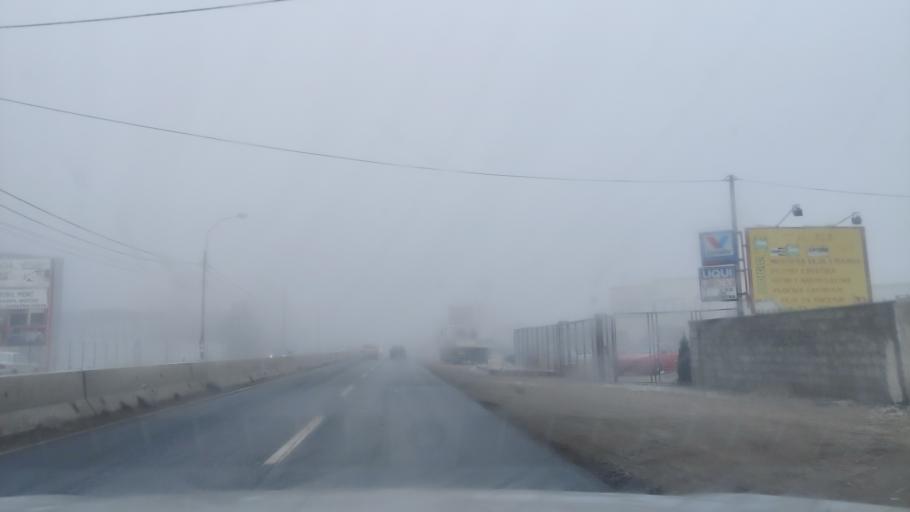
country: RS
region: Central Serbia
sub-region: Belgrade
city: Stari Grad
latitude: 44.8738
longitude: 20.4701
